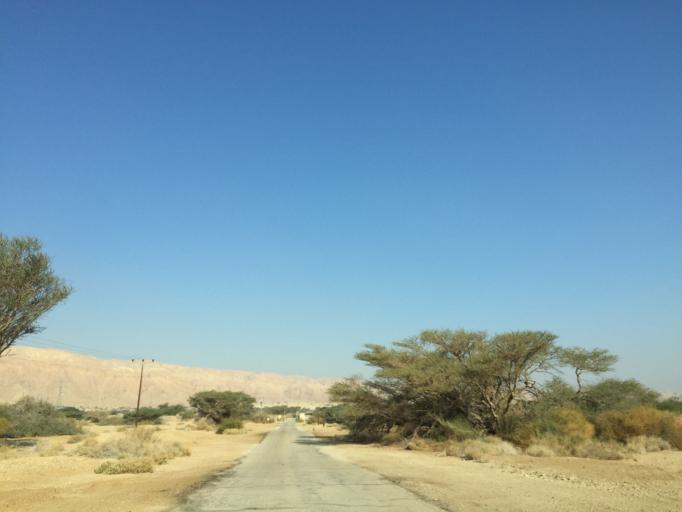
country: JO
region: Ma'an
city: Al Quwayrah
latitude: 29.8436
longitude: 35.0293
